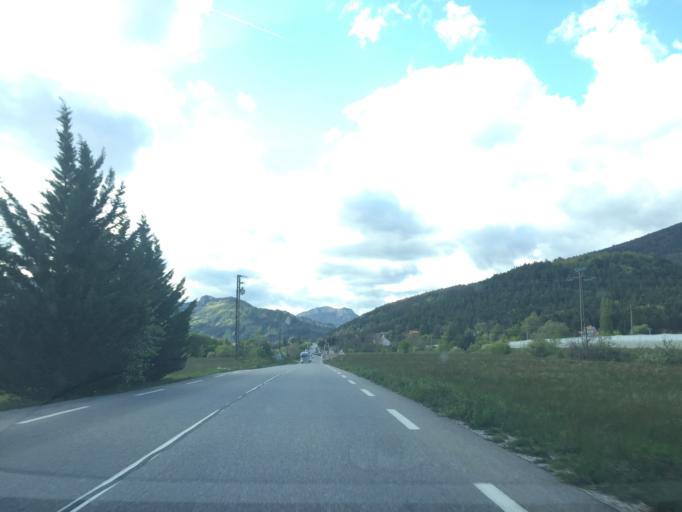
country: FR
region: Provence-Alpes-Cote d'Azur
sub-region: Departement des Hautes-Alpes
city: Serres
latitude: 44.4072
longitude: 5.7288
